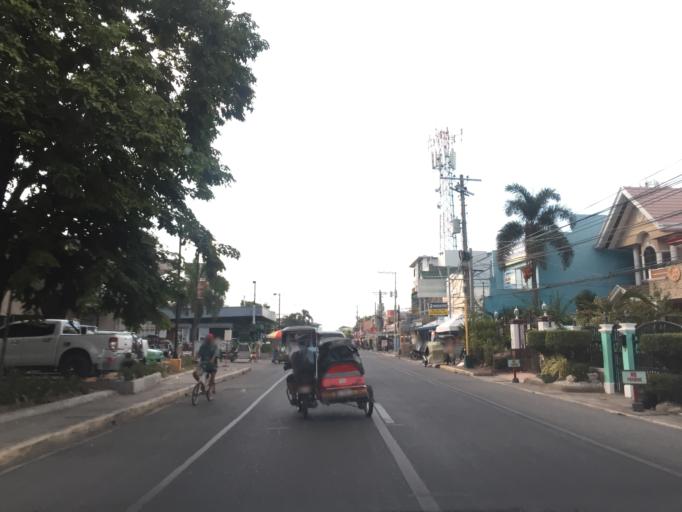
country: PH
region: Ilocos
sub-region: Province of Pangasinan
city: Bolingit
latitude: 15.9328
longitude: 120.3477
